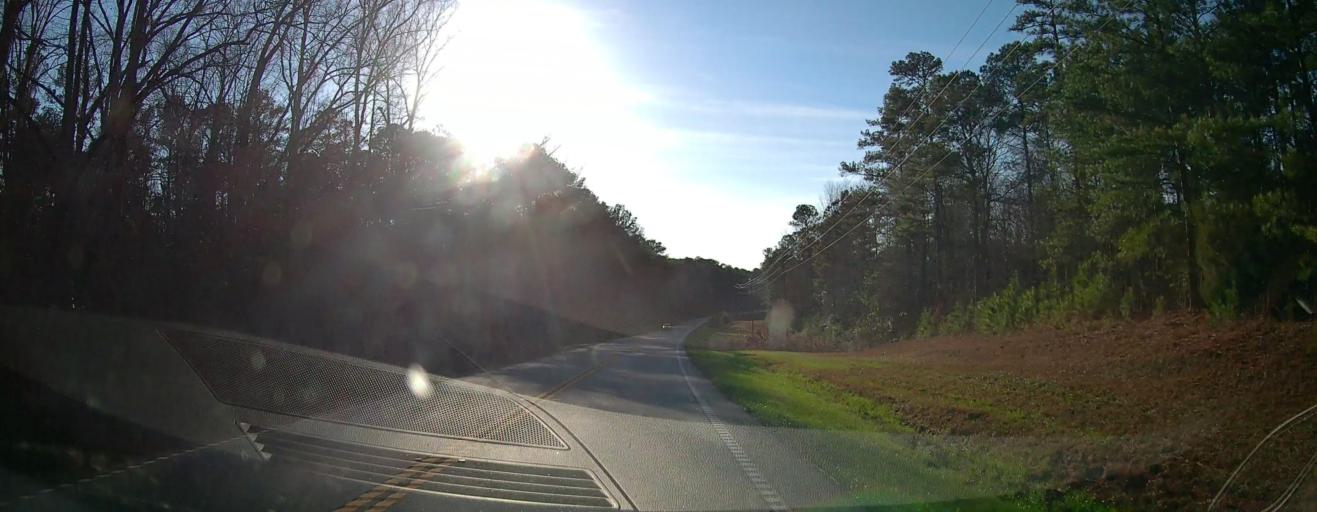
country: US
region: Alabama
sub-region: Chambers County
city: Valley
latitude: 32.7428
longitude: -85.0408
